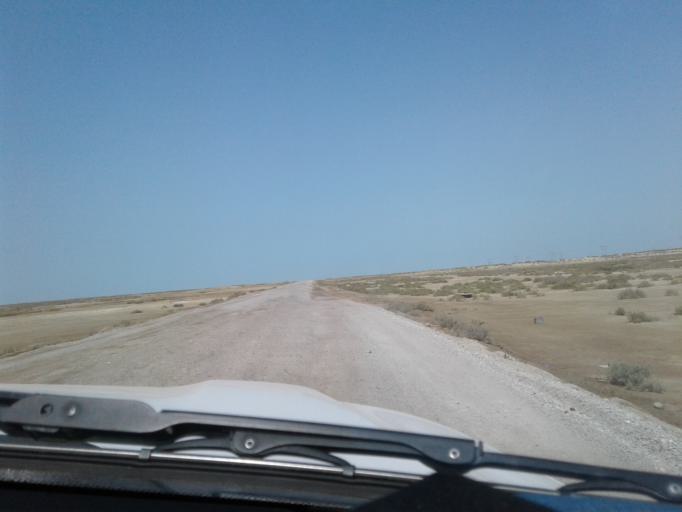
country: IR
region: Golestan
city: Gomishan
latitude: 37.8360
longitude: 53.9052
